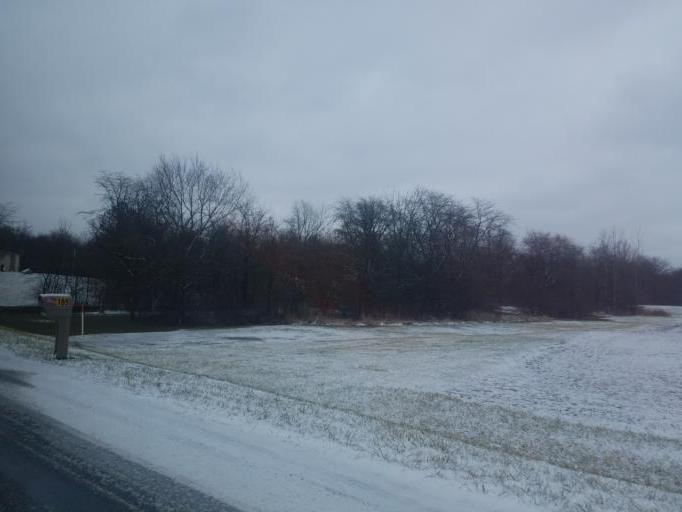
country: US
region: Ohio
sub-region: Delaware County
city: Sunbury
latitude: 40.2052
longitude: -82.7748
